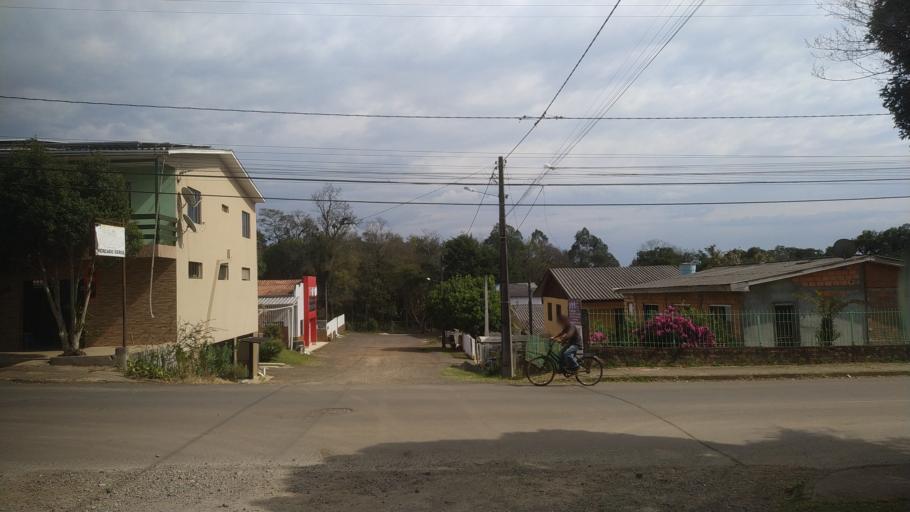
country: BR
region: Santa Catarina
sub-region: Chapeco
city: Chapeco
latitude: -27.1332
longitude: -52.6193
